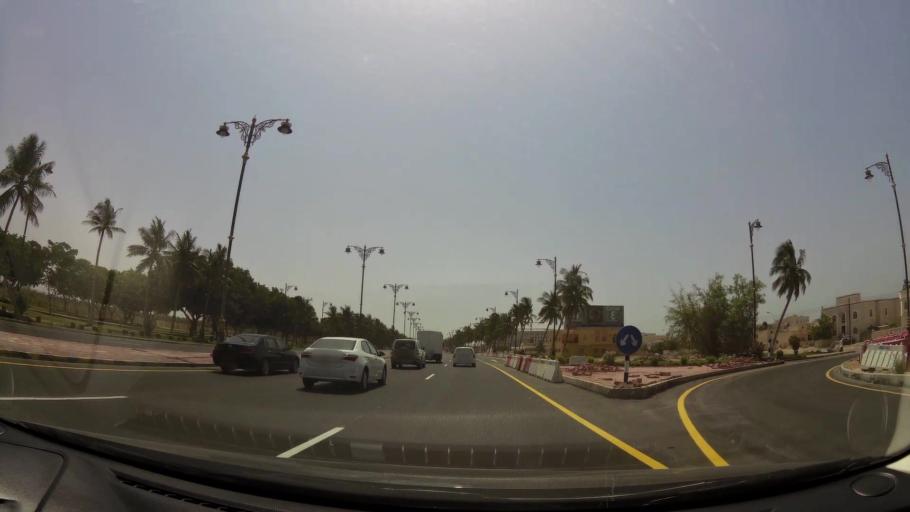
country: OM
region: Zufar
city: Salalah
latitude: 17.0231
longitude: 54.1045
